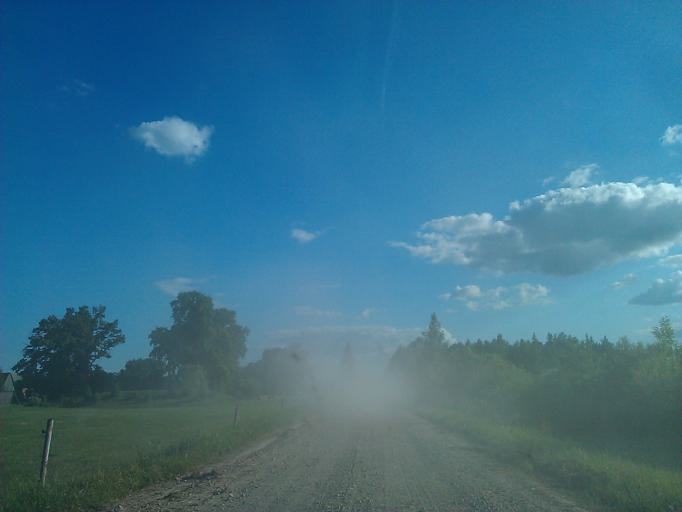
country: LV
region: Varaklani
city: Varaklani
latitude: 56.5763
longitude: 26.7925
